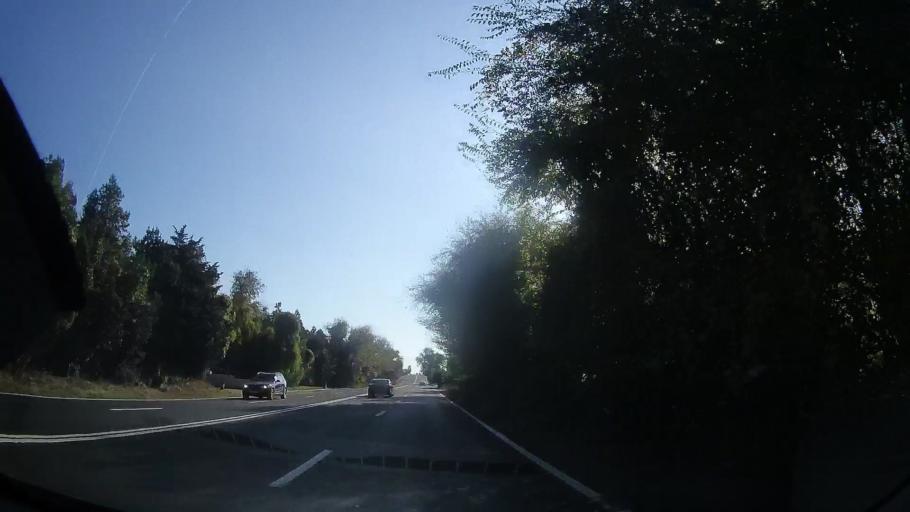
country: RO
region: Constanta
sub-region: Comuna Douazeci si Trei August
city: Dulcesti
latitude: 43.8634
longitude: 28.5752
